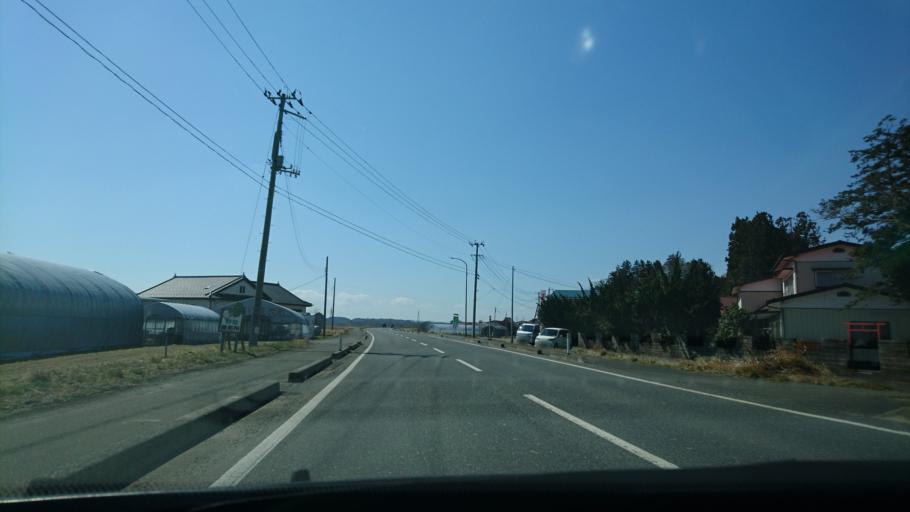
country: JP
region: Iwate
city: Ichinoseki
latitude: 38.7444
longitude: 141.1312
